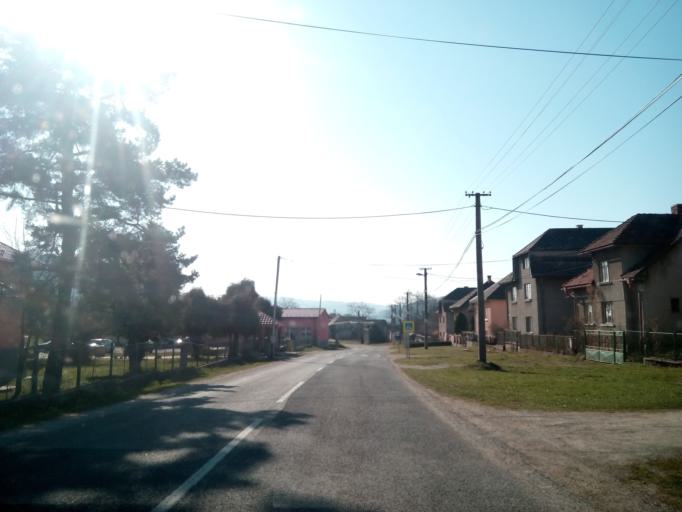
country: SK
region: Kosicky
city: Dobsina
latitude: 48.7143
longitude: 20.2781
